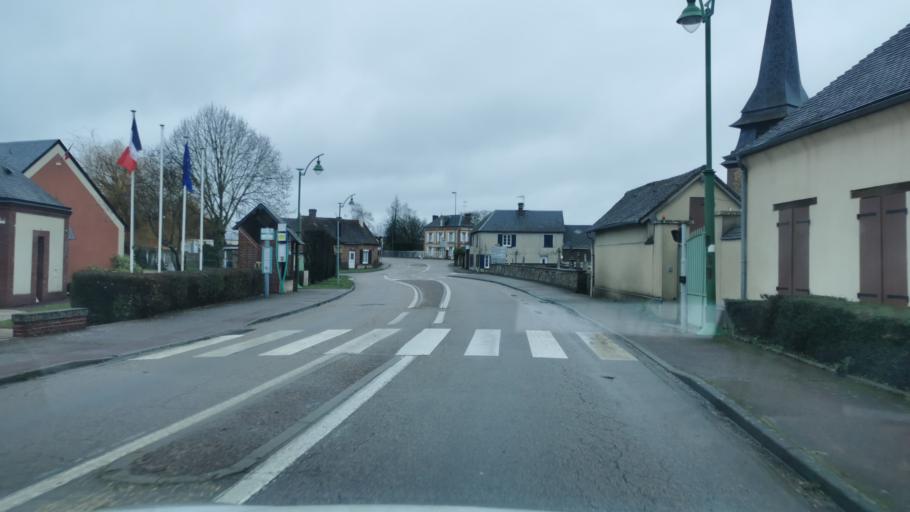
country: FR
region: Haute-Normandie
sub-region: Departement de l'Eure
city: Normanville
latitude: 49.0815
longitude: 1.1812
